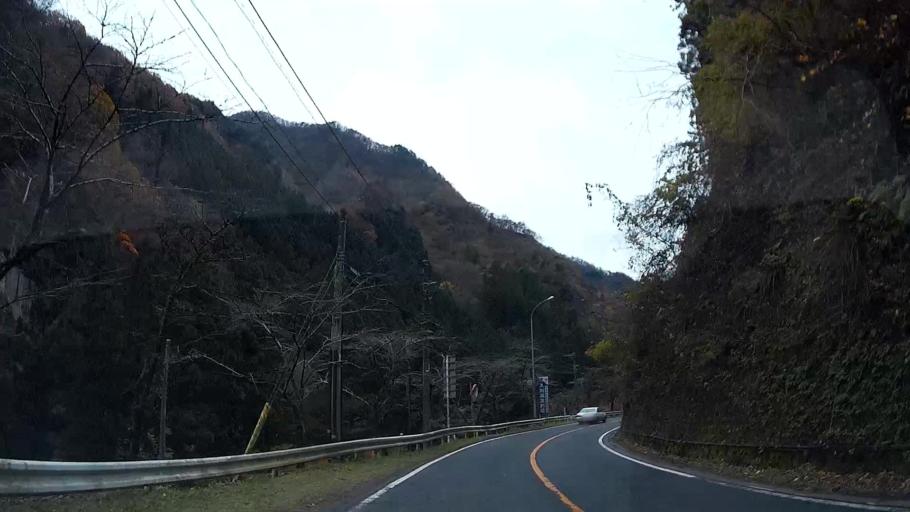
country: JP
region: Saitama
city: Chichibu
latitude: 35.9429
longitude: 138.9664
